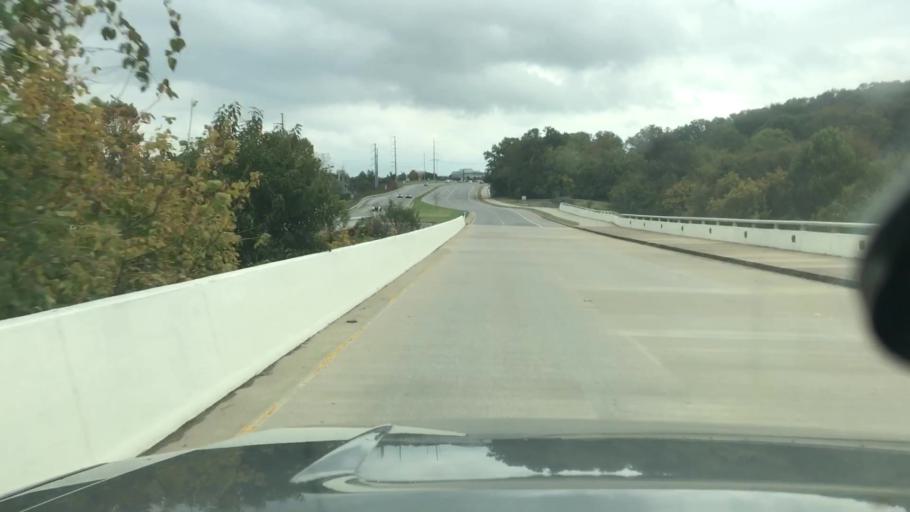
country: US
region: Tennessee
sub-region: Williamson County
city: Franklin
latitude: 35.9437
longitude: -86.8451
